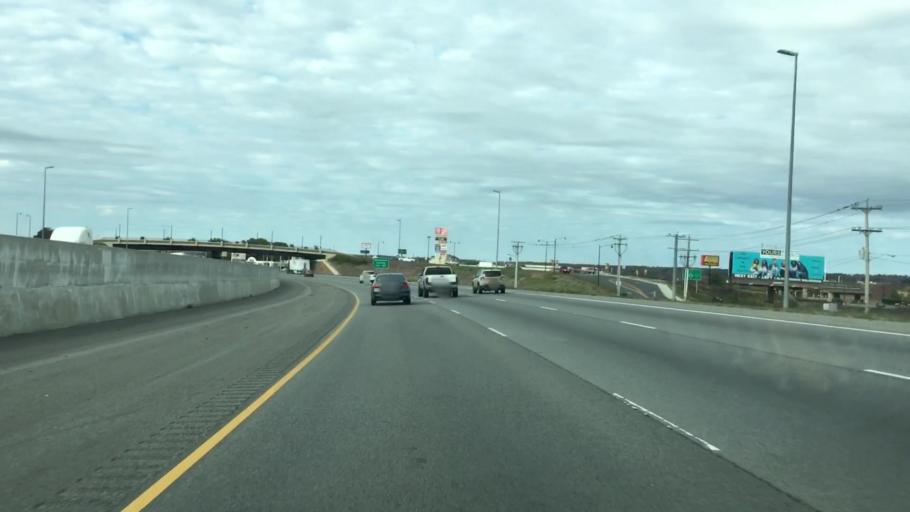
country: US
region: Arkansas
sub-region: Faulkner County
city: Conway
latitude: 35.0820
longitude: -92.4138
